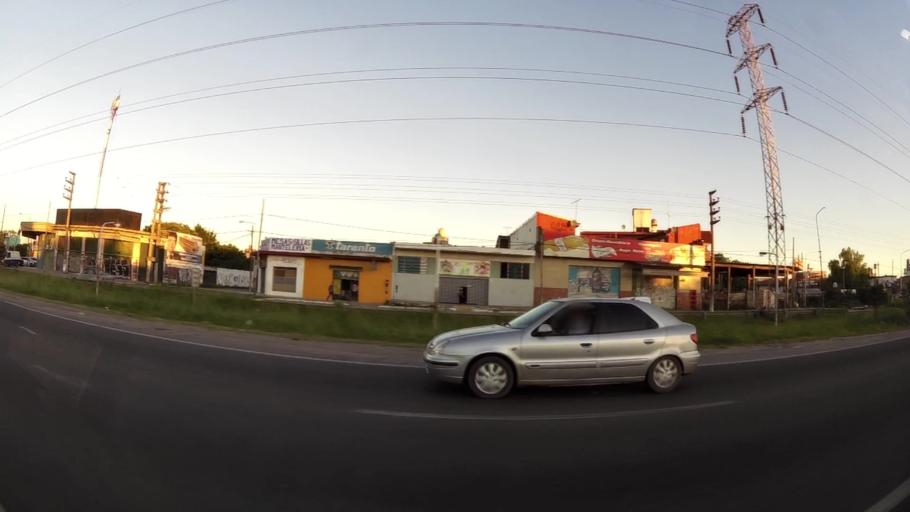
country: AR
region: Buenos Aires
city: Pontevedra
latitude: -34.7730
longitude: -58.6212
